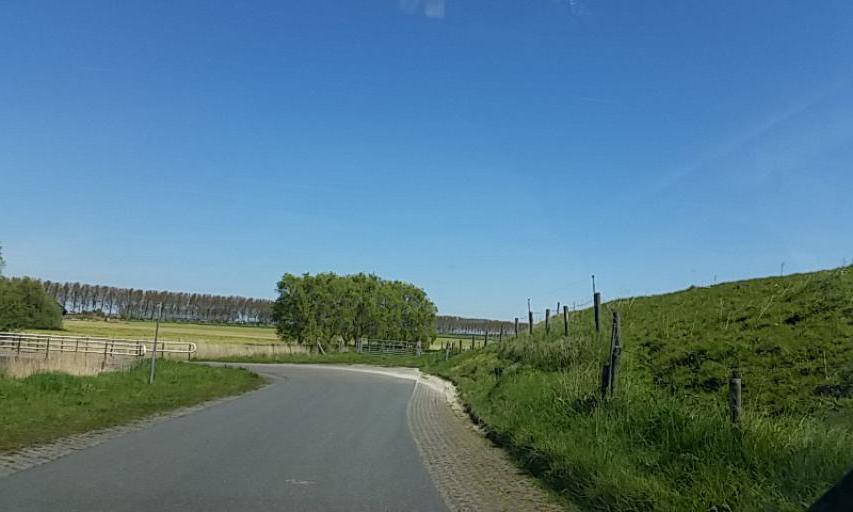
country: NL
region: Zeeland
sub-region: Gemeente Borsele
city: Borssele
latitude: 51.3299
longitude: 3.7185
